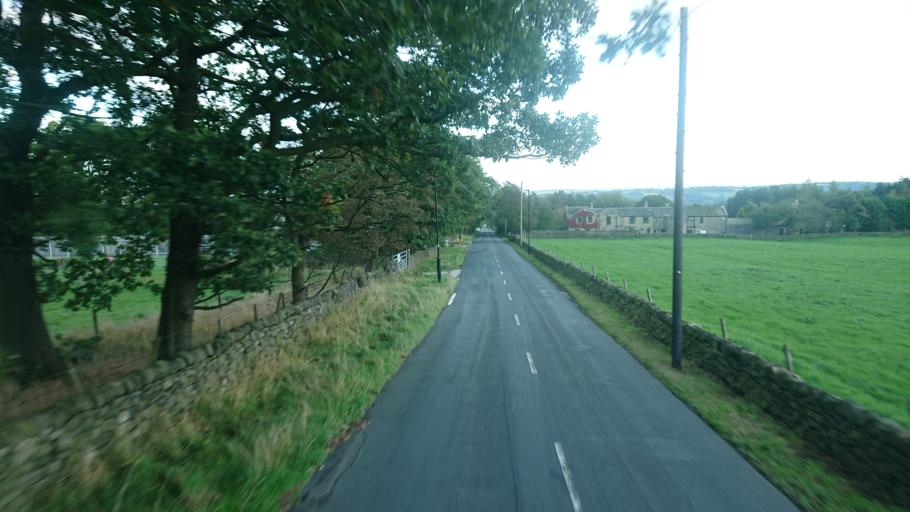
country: GB
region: England
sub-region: Derbyshire
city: Dronfield
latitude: 53.3399
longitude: -1.5550
